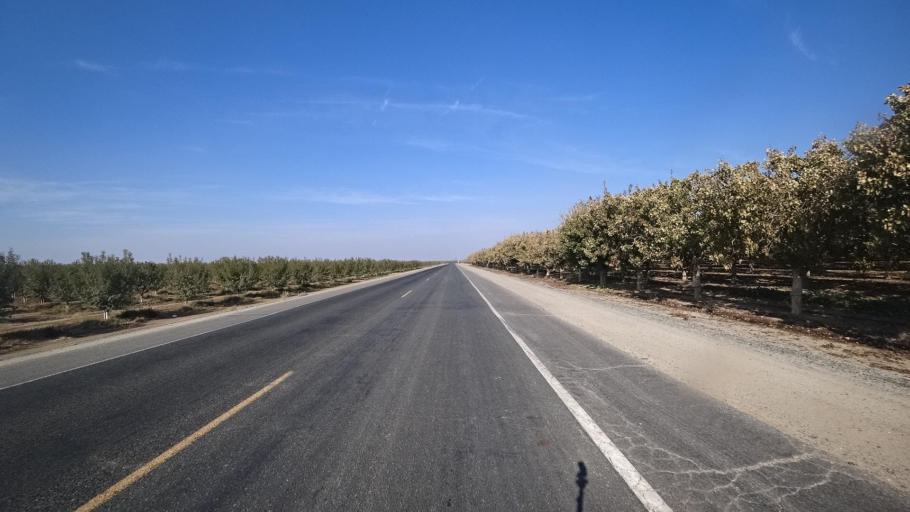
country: US
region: California
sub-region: Kern County
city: McFarland
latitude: 35.6533
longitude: -119.1957
